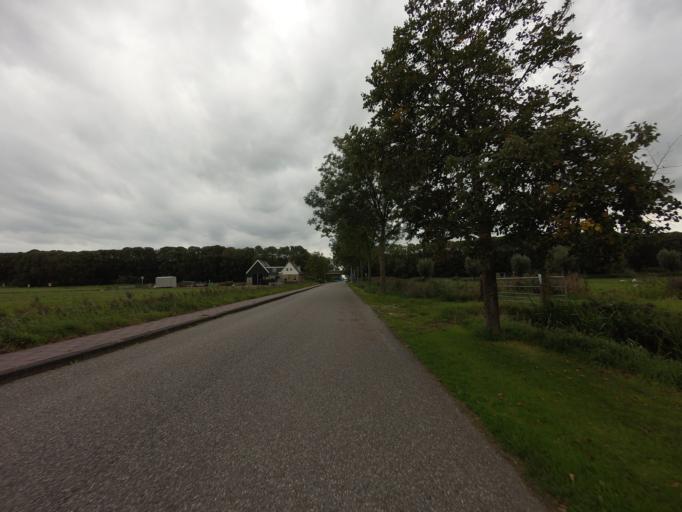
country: NL
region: Friesland
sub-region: Sudwest Fryslan
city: Bolsward
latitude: 53.0485
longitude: 5.5753
